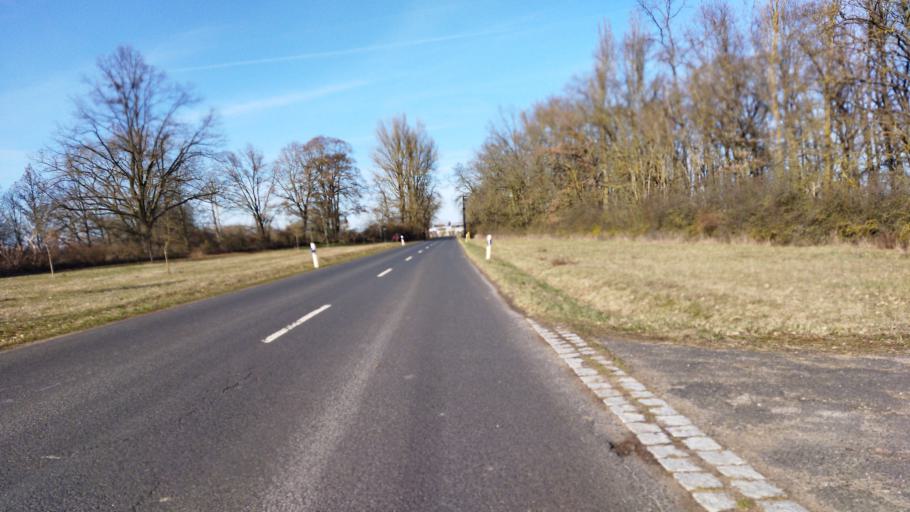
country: DE
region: Bavaria
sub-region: Regierungsbezirk Unterfranken
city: Grafenrheinfeld
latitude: 49.9892
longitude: 10.1995
